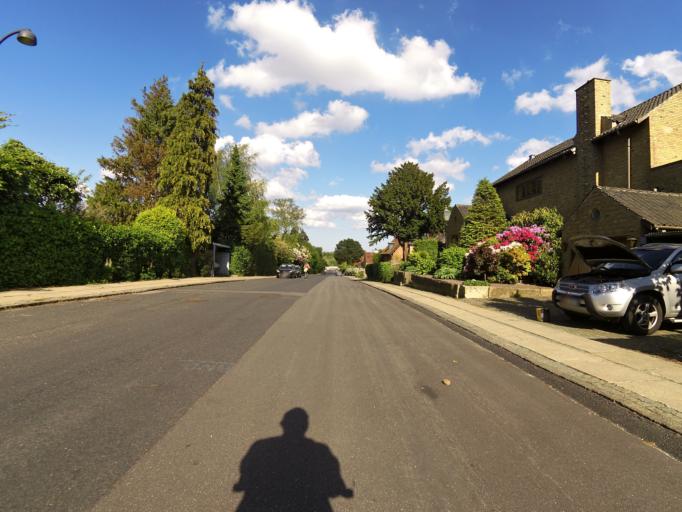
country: DK
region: Capital Region
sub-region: Lyngby-Tarbaek Kommune
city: Kongens Lyngby
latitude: 55.7447
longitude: 12.5268
